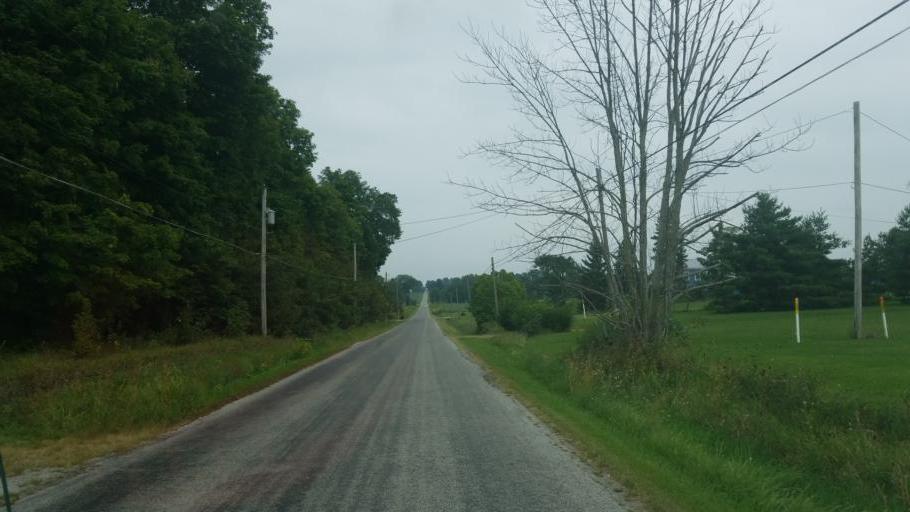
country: US
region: Ohio
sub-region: Wayne County
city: Creston
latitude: 40.9599
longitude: -81.9160
